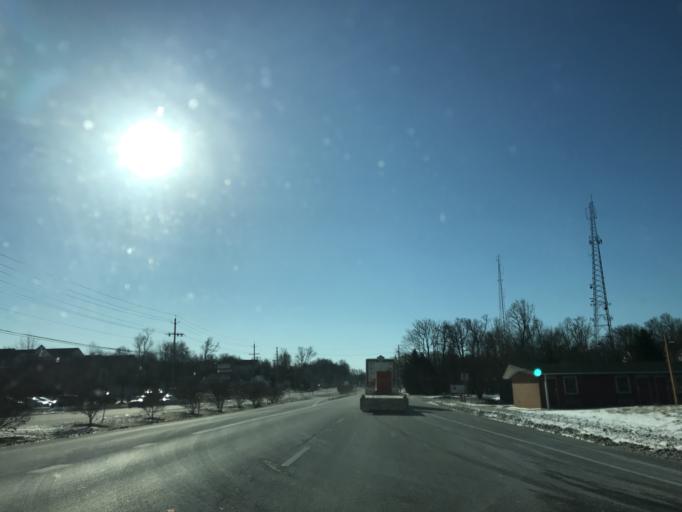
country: US
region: Maryland
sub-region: Charles County
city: La Plata
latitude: 38.5282
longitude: -76.9828
